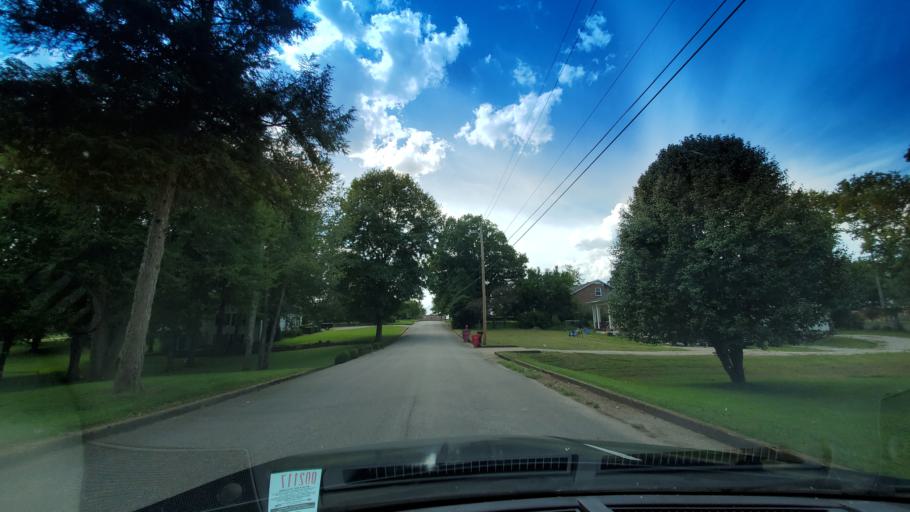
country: US
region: Tennessee
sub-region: Smith County
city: Carthage
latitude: 36.2555
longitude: -85.9495
